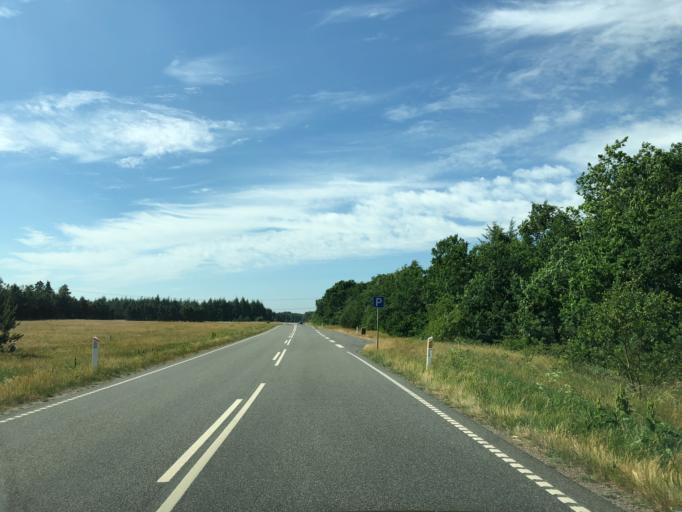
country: DK
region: Central Jutland
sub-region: Ikast-Brande Kommune
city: Brande
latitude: 55.9124
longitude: 9.1817
